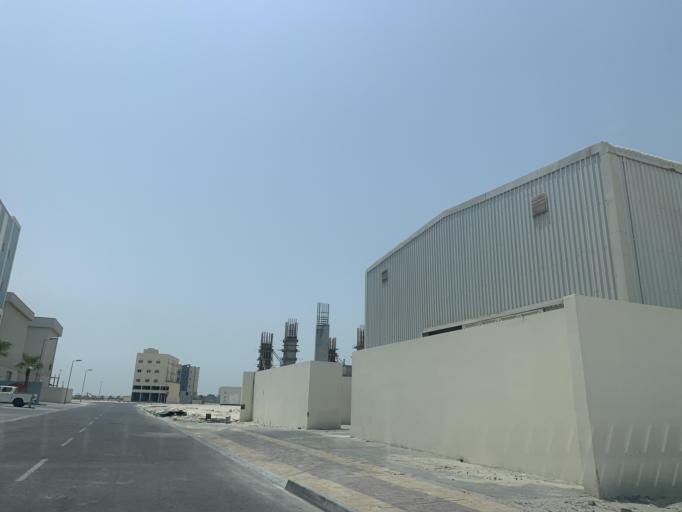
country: BH
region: Muharraq
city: Al Hadd
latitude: 26.2615
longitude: 50.6689
